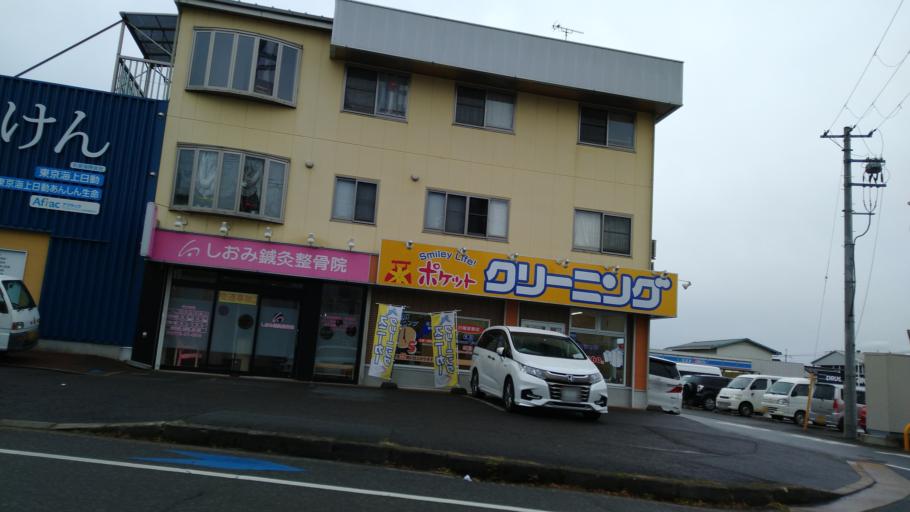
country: JP
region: Kyoto
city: Fukuchiyama
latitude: 35.2967
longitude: 135.1599
